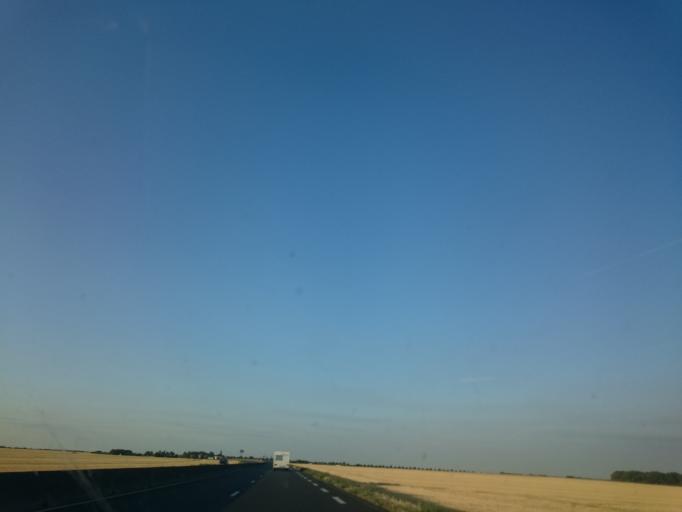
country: FR
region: Ile-de-France
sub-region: Departement de l'Essonne
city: Angerville
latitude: 48.3340
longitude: 2.0324
